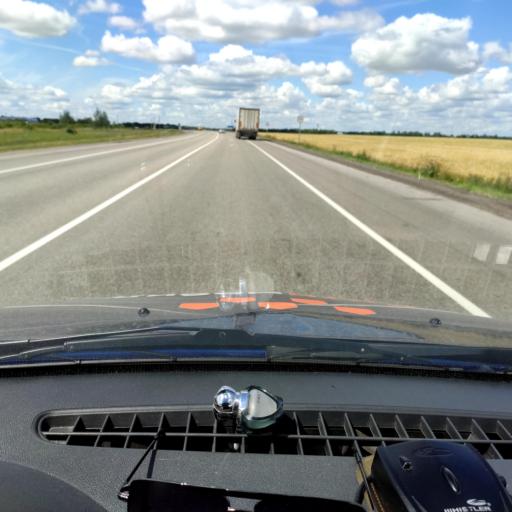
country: RU
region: Lipetsk
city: Borinskoye
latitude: 52.4744
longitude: 39.3781
